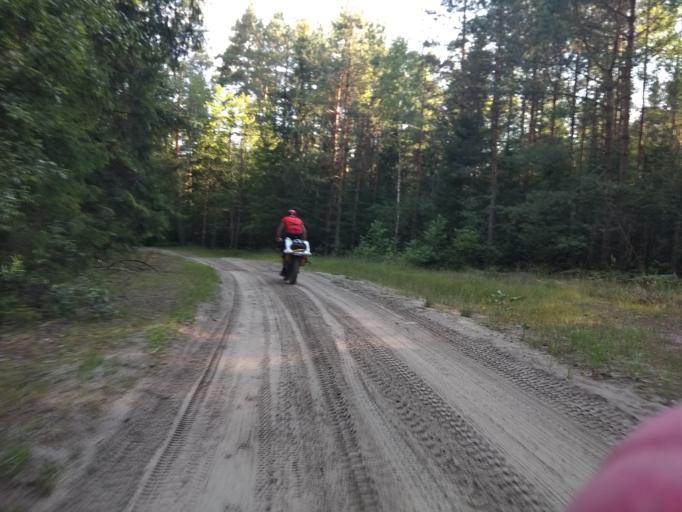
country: RU
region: Moskovskaya
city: Misheronskiy
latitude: 55.7364
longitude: 39.7708
